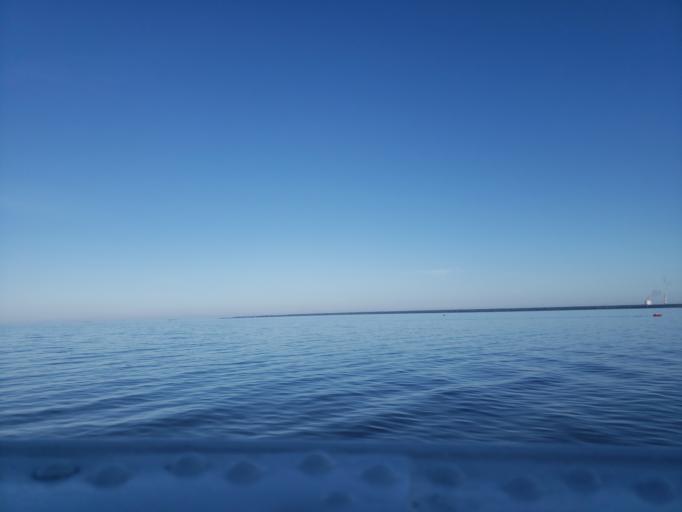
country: RU
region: St.-Petersburg
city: Ol'gino
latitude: 59.9428
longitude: 30.0992
